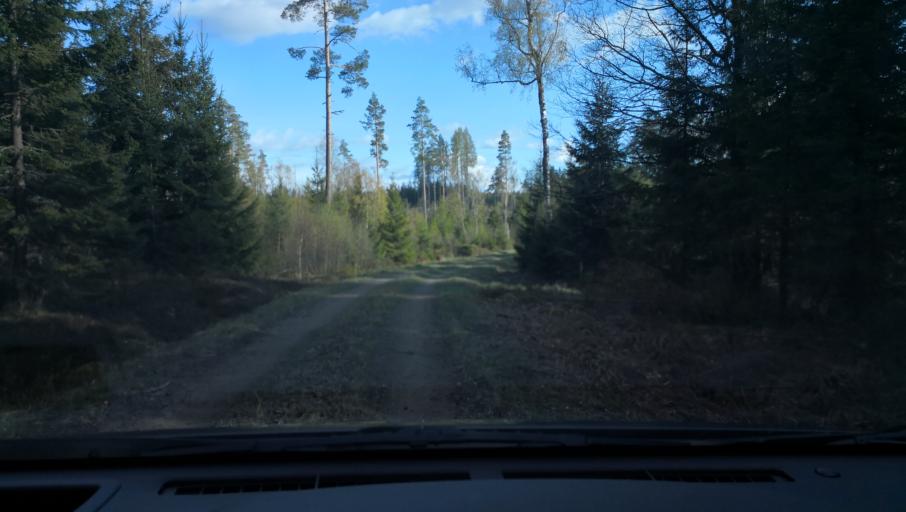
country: SE
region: OErebro
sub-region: Askersunds Kommun
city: Asbro
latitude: 58.8697
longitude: 15.1273
